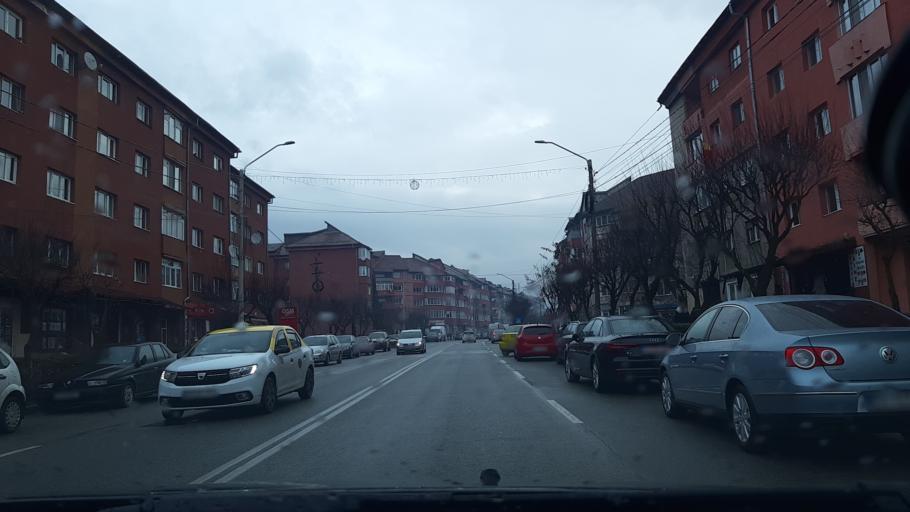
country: RO
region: Hunedoara
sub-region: Municipiul Petrosani
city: Petrosani
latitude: 45.4455
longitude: 23.3813
